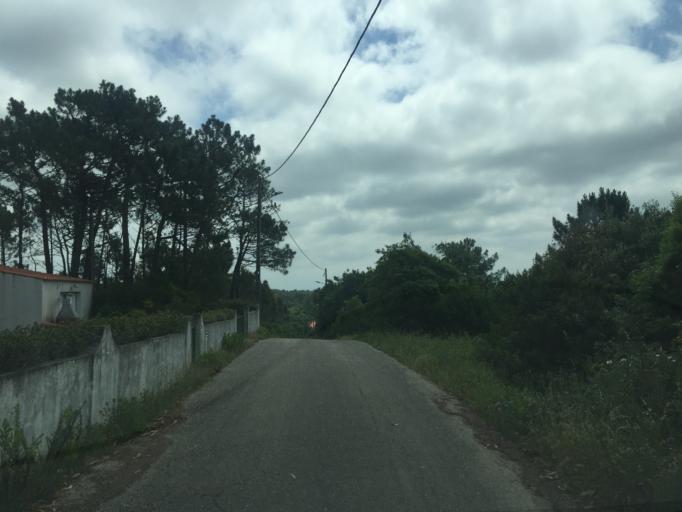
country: PT
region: Coimbra
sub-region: Figueira da Foz
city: Tavarede
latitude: 40.1865
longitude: -8.8277
